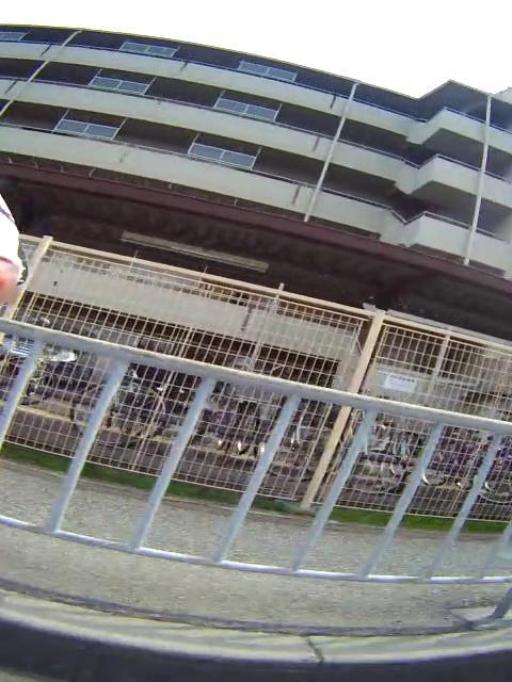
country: JP
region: Osaka
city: Toyonaka
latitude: 34.7886
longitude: 135.4727
